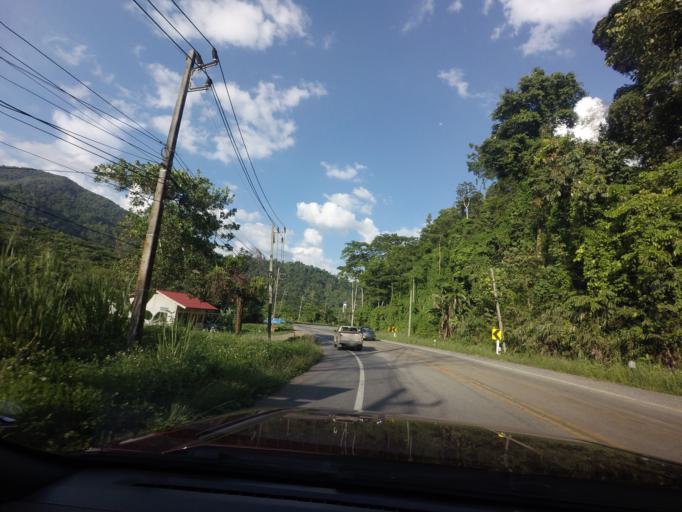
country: TH
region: Yala
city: Than To
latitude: 6.2015
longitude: 101.1726
